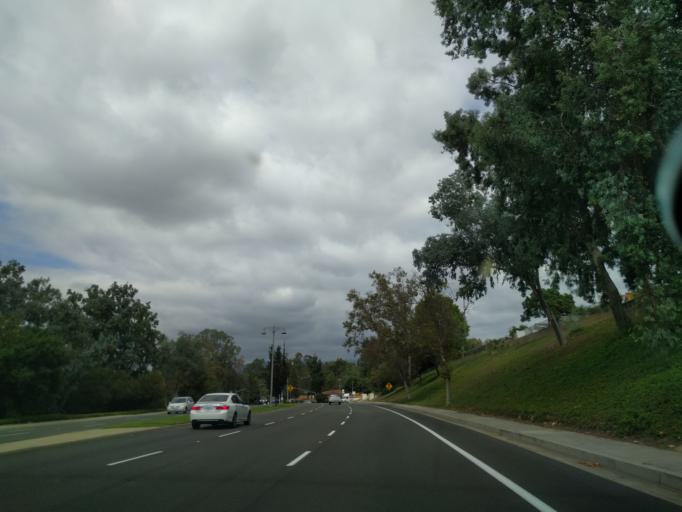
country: US
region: California
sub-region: Orange County
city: Mission Viejo
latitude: 33.6276
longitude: -117.6670
